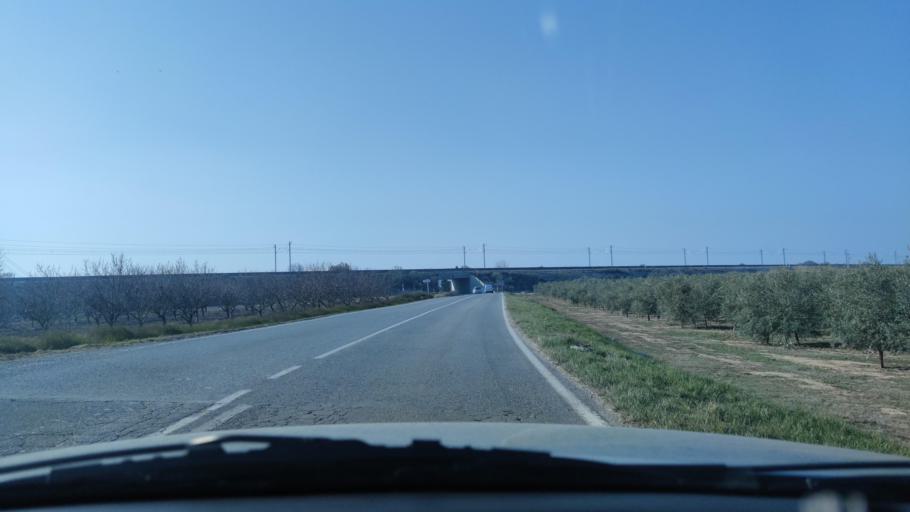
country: ES
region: Catalonia
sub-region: Provincia de Lleida
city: Juneda
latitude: 41.5563
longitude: 0.7410
